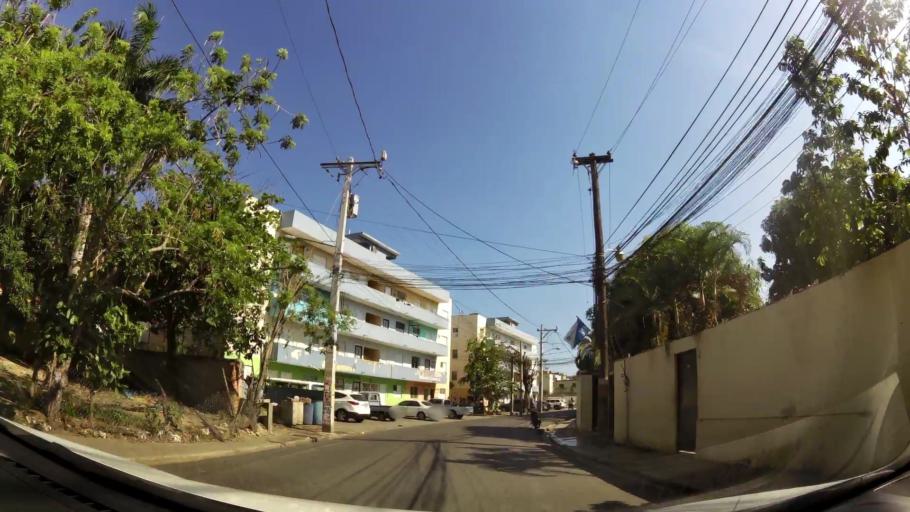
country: DO
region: Santo Domingo
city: Santo Domingo Oeste
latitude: 18.4661
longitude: -69.9983
